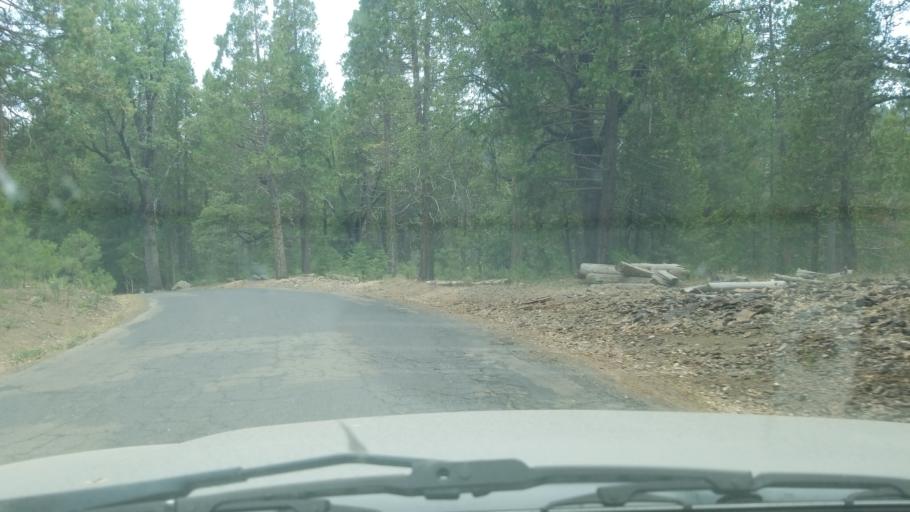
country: US
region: California
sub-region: Mariposa County
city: Yosemite Valley
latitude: 37.8645
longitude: -119.8689
